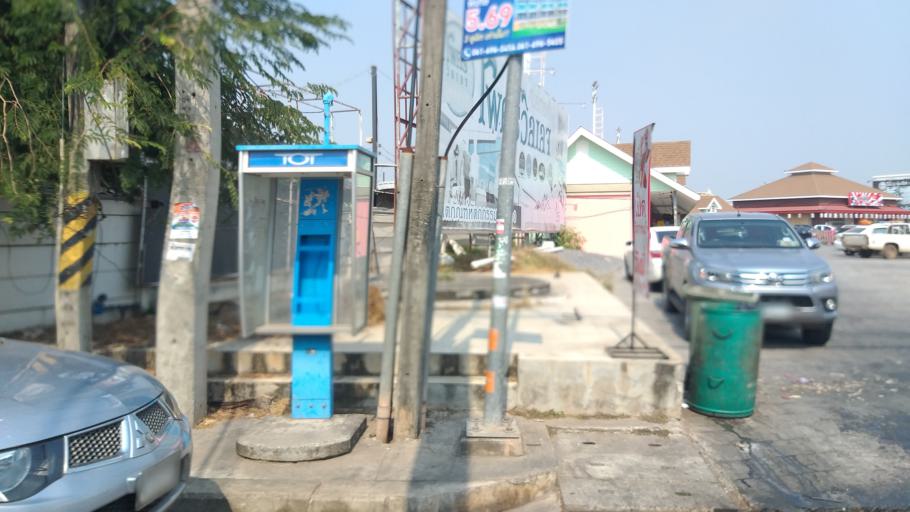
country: TH
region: Changwat Udon Thani
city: Udon Thani
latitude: 17.4148
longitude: 102.7751
